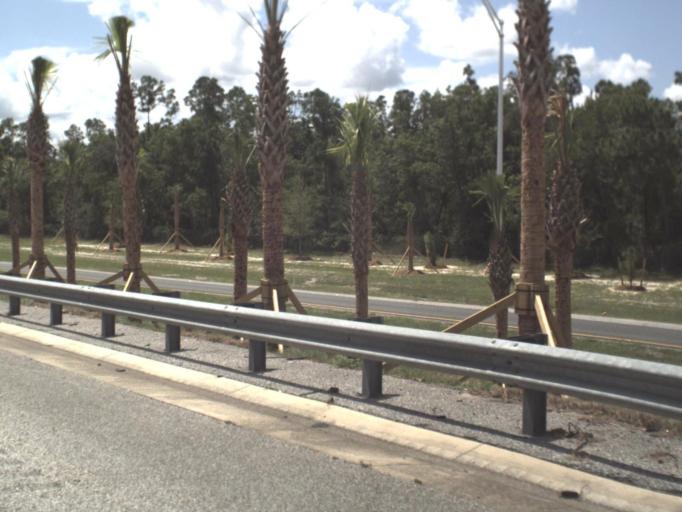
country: US
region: Florida
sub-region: Flagler County
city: Palm Coast
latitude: 29.6612
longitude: -81.2858
